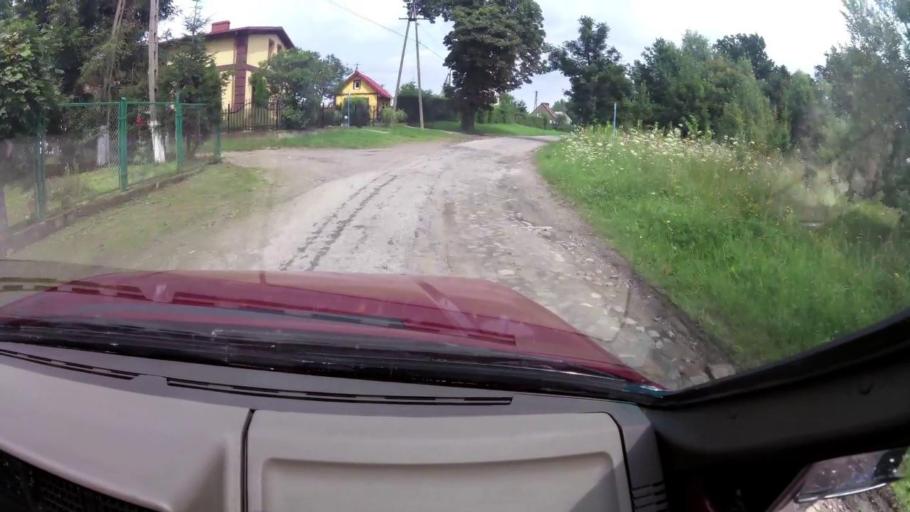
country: PL
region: West Pomeranian Voivodeship
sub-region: Powiat swidwinski
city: Polczyn-Zdroj
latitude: 53.7950
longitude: 16.0436
